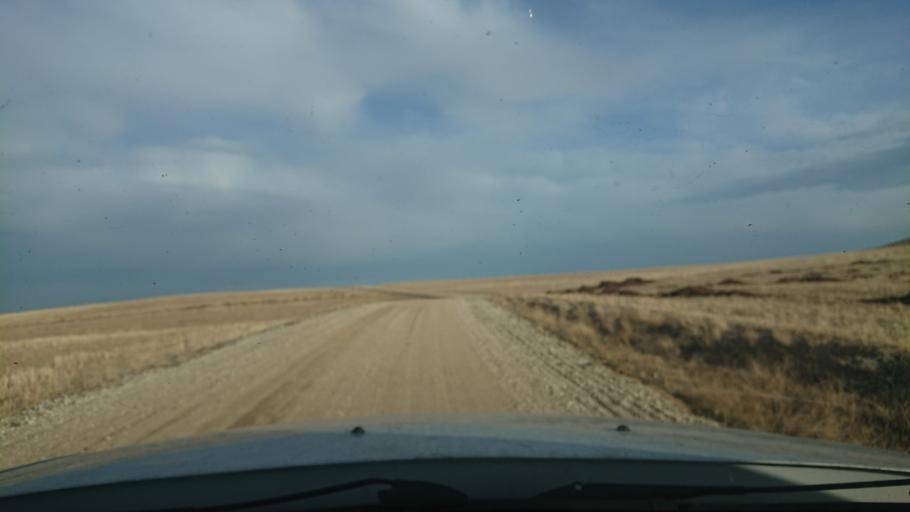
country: TR
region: Aksaray
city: Ortakoy
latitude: 38.7013
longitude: 33.8734
